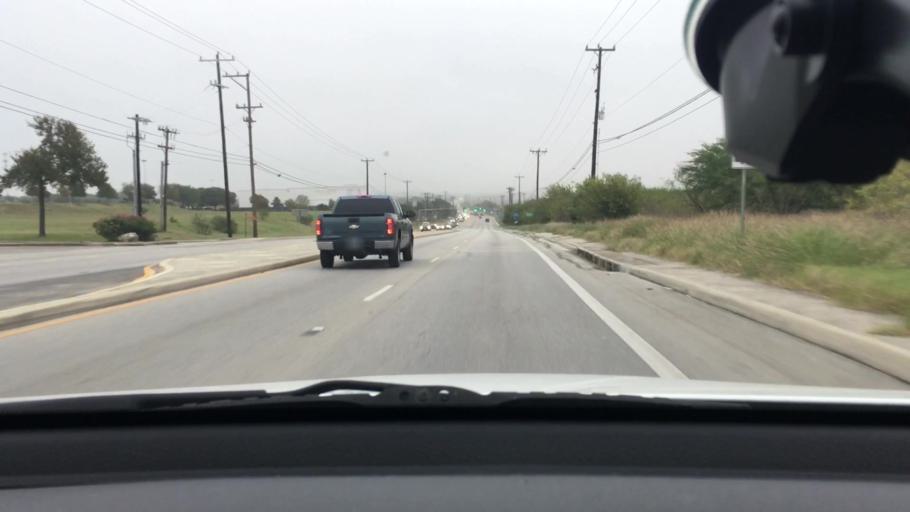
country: US
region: Texas
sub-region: Bexar County
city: Live Oak
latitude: 29.5927
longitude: -98.3501
